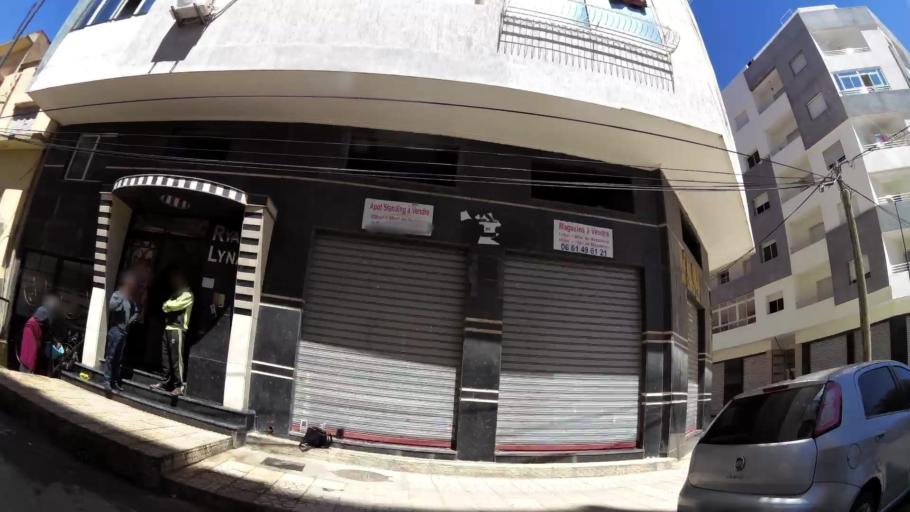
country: MA
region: Meknes-Tafilalet
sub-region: Meknes
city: Meknes
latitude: 33.9056
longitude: -5.5310
